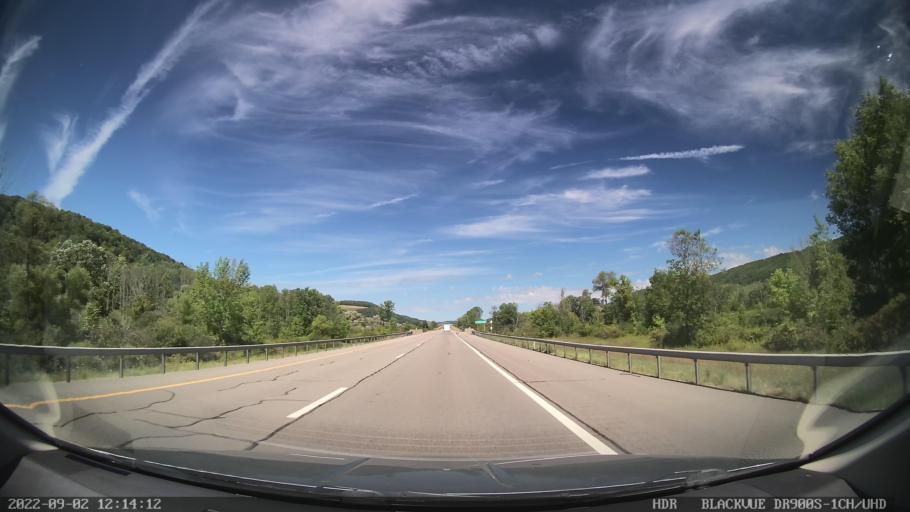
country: US
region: New York
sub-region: Steuben County
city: Wayland
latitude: 42.4485
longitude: -77.4735
